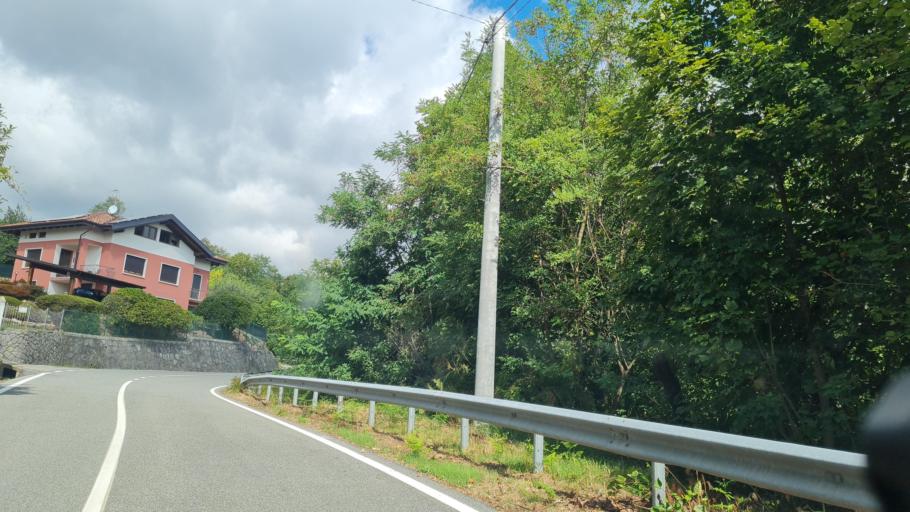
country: IT
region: Piedmont
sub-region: Provincia di Biella
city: Fontanella-Ozino
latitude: 45.6245
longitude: 8.1673
